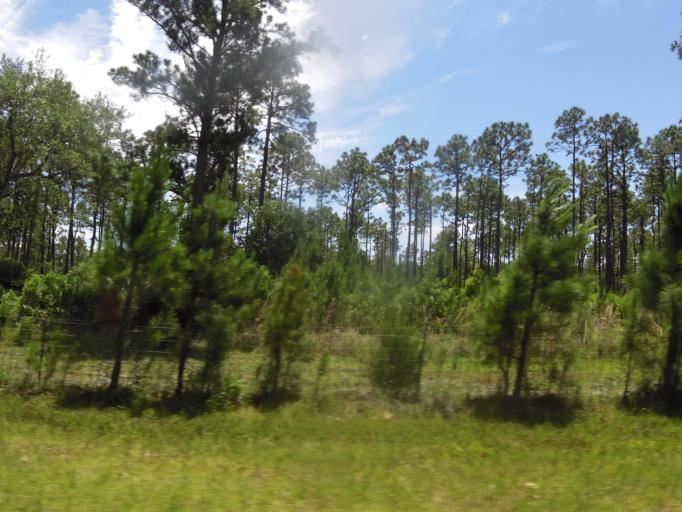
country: US
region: Florida
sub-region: Duval County
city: Atlantic Beach
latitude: 30.4595
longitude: -81.5067
